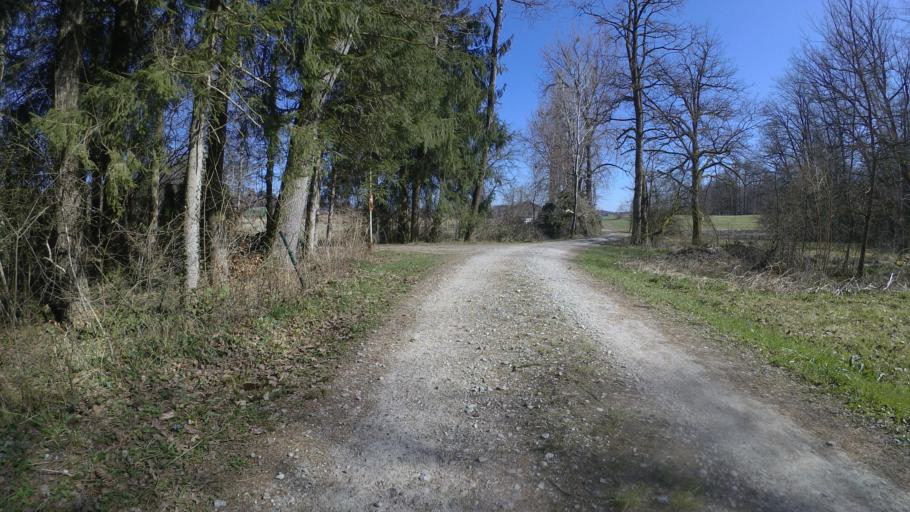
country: DE
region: Bavaria
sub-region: Upper Bavaria
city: Seeon-Seebruck
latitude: 47.9650
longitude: 12.4886
